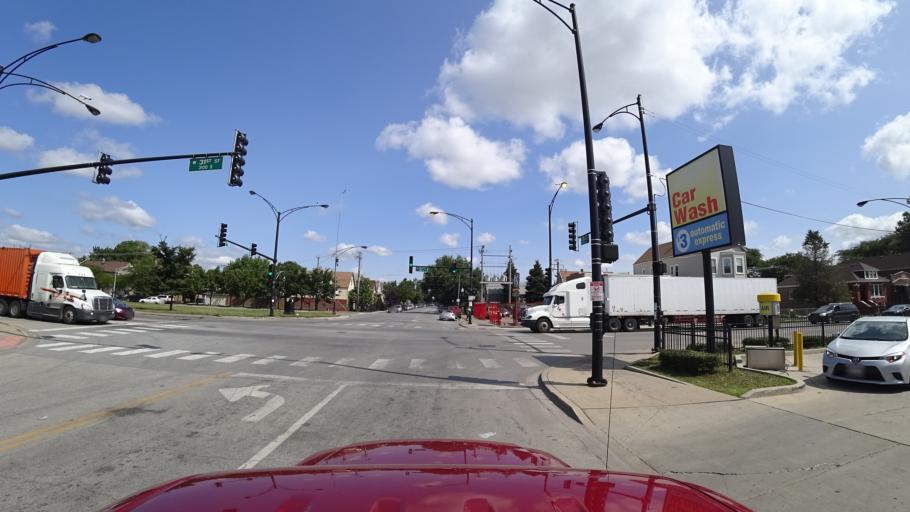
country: US
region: Illinois
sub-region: Cook County
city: Cicero
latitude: 41.8366
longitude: -87.7340
